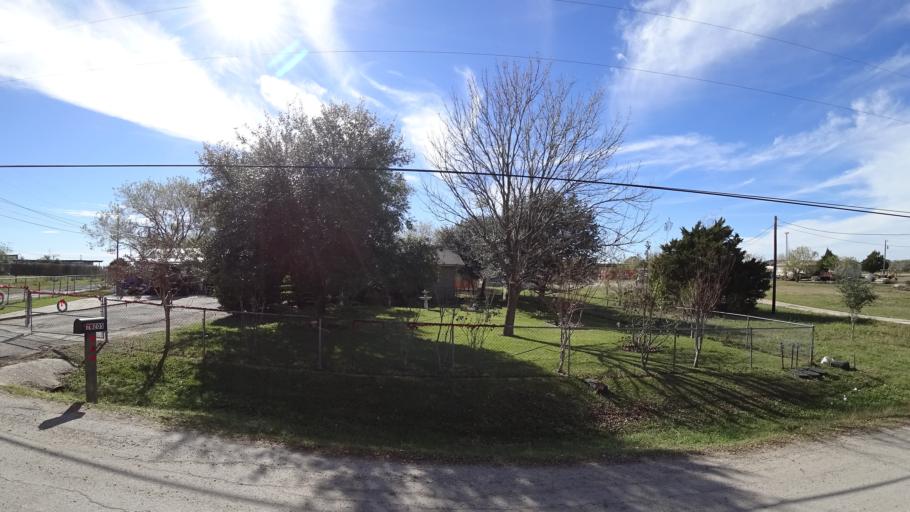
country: US
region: Texas
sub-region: Travis County
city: Onion Creek
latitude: 30.1159
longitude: -97.6977
